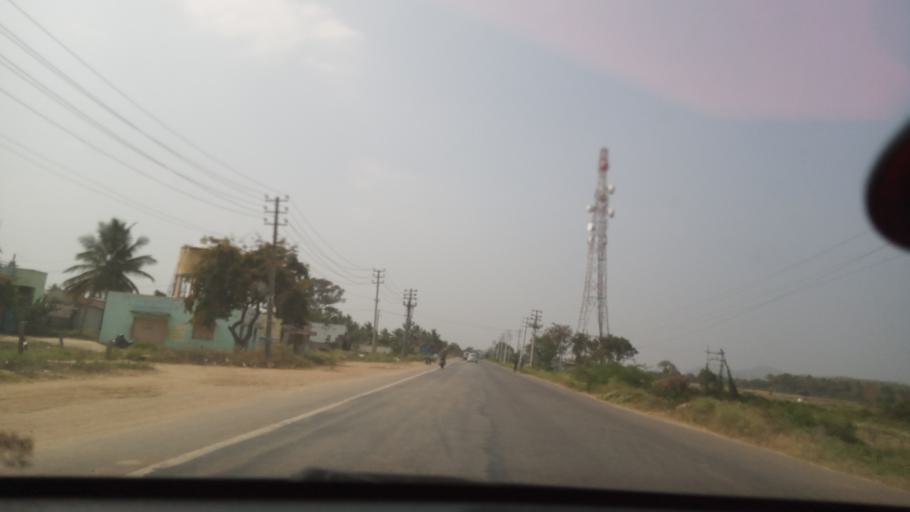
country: IN
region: Karnataka
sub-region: Chamrajnagar
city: Chamrajnagar
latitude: 11.9902
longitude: 76.8671
